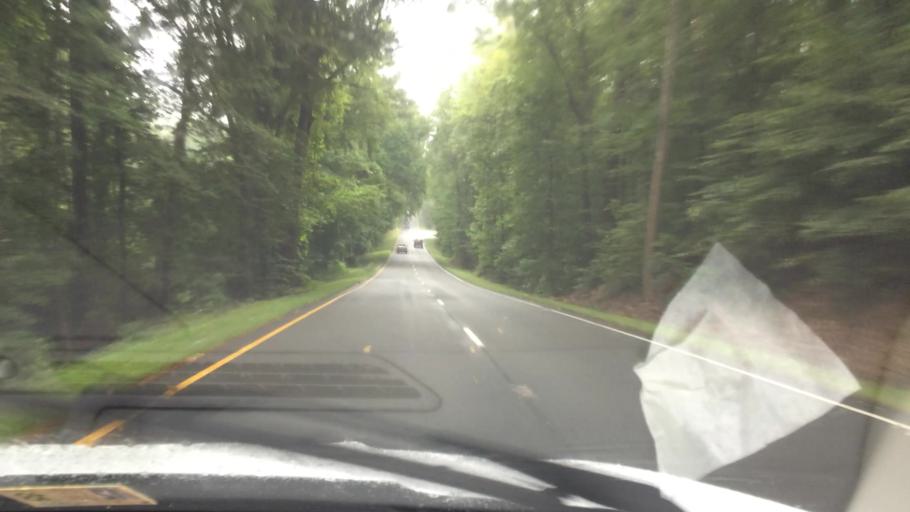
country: US
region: Virginia
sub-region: James City County
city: Williamsburg
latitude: 37.3964
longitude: -76.7857
